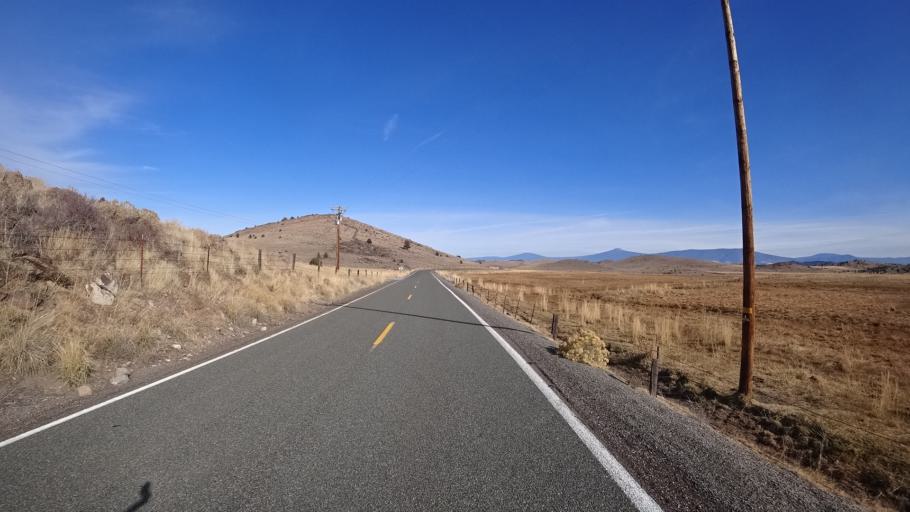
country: US
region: California
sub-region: Siskiyou County
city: Weed
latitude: 41.5379
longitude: -122.5043
